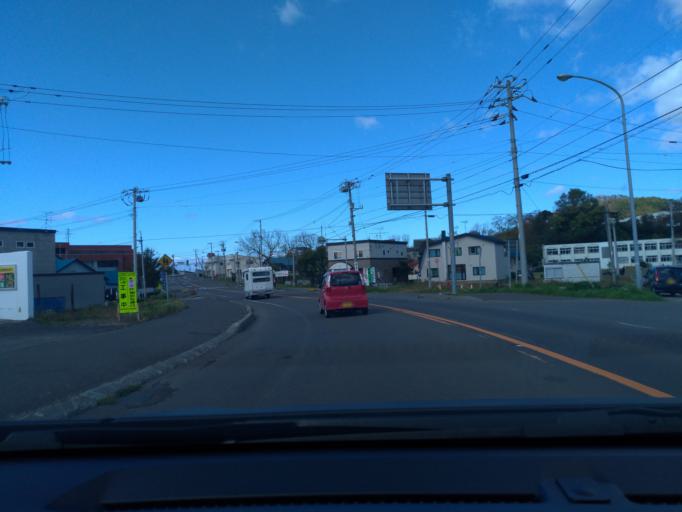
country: JP
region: Hokkaido
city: Ishikari
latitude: 43.3992
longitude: 141.4360
